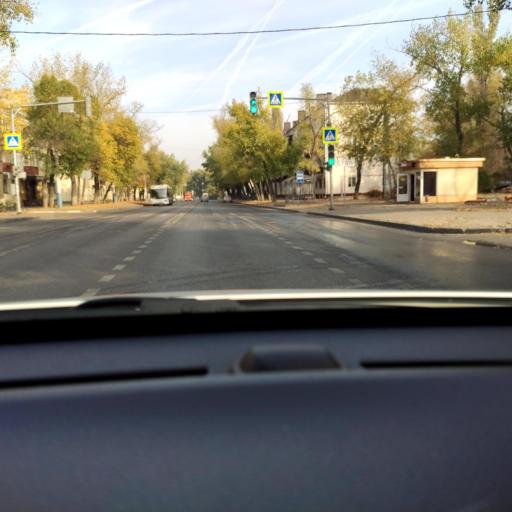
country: RU
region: Voronezj
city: Somovo
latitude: 51.7159
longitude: 39.2745
